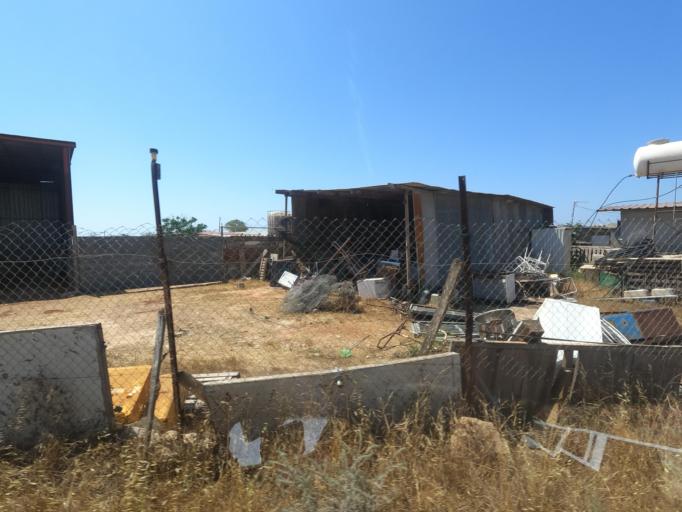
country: CY
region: Ammochostos
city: Liopetri
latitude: 35.0219
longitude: 33.8808
